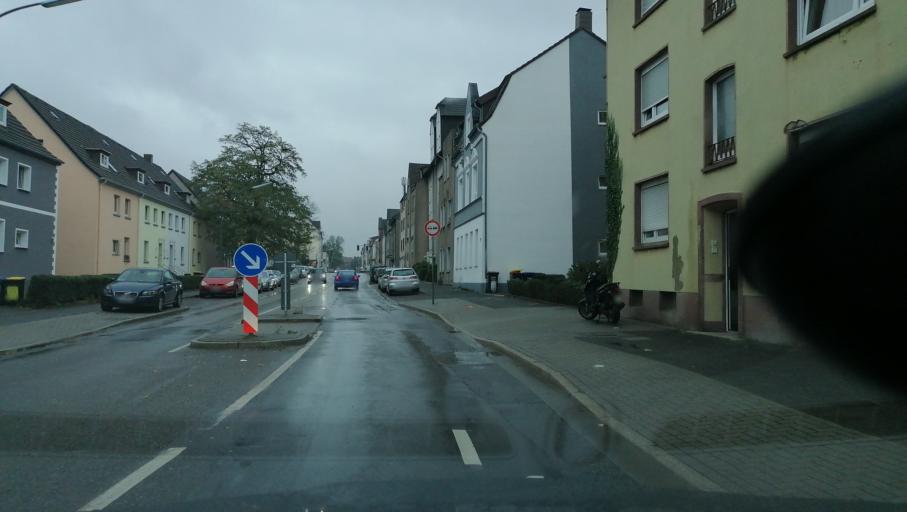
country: DE
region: North Rhine-Westphalia
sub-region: Regierungsbezirk Munster
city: Recklinghausen
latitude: 51.5746
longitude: 7.2008
